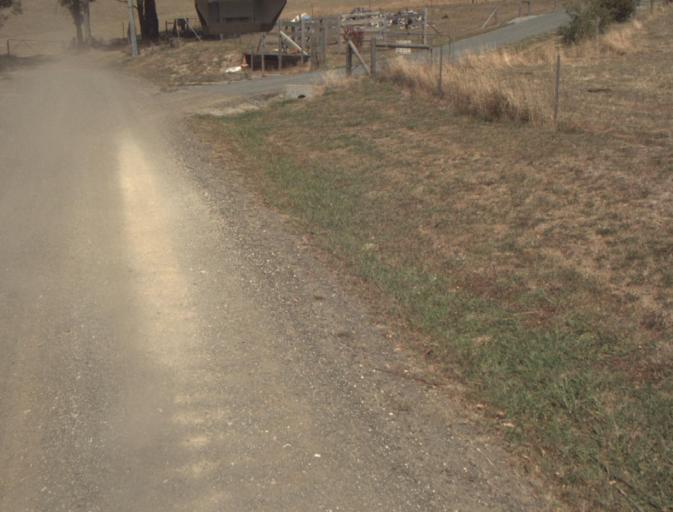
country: AU
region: Tasmania
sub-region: Launceston
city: Mayfield
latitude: -41.2597
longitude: 147.1456
